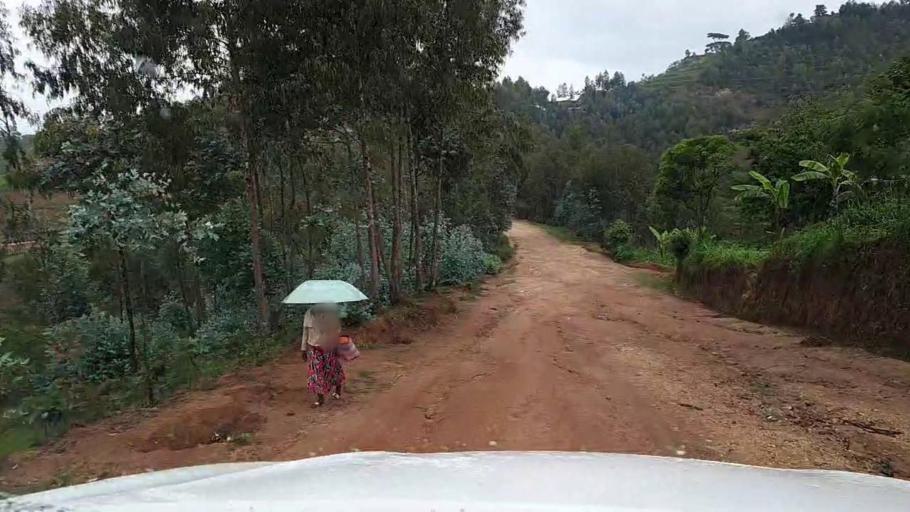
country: RW
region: Southern Province
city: Nzega
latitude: -2.4607
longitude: 29.4939
